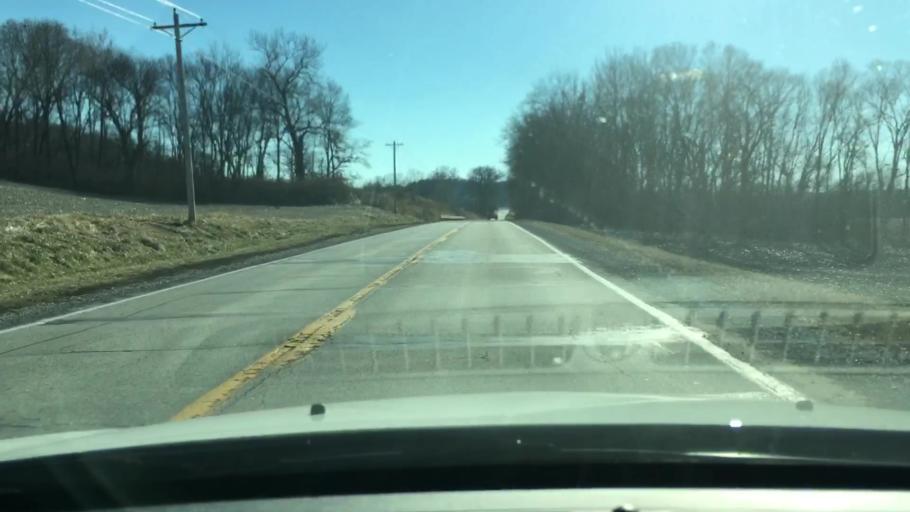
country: US
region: Illinois
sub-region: Morgan County
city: Meredosia
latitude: 39.7184
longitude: -90.5685
